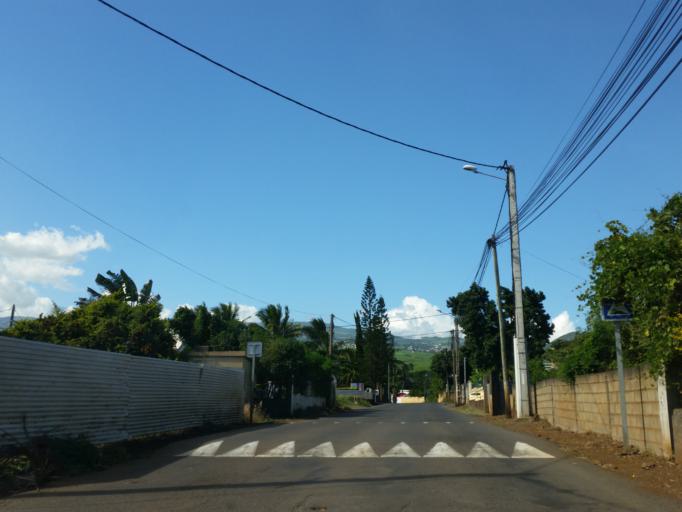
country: RE
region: Reunion
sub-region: Reunion
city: Saint-Pierre
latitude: -21.3281
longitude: 55.4913
